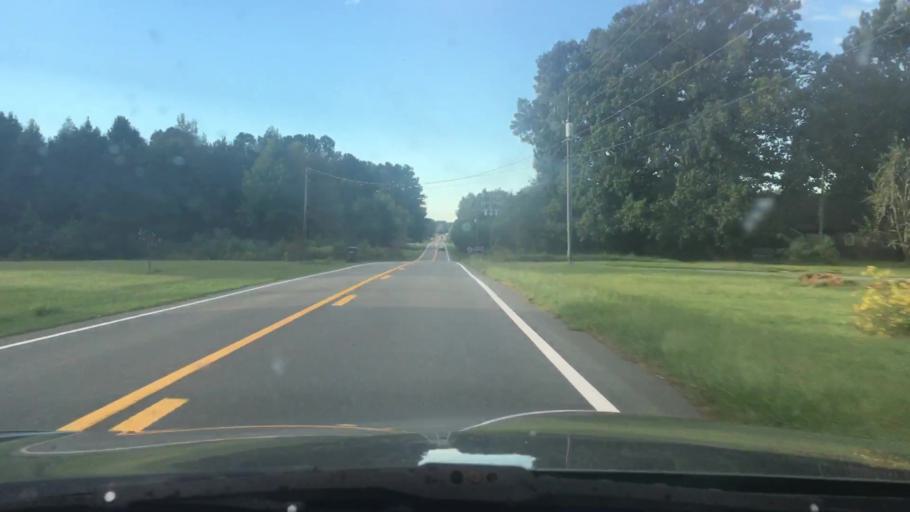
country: US
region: North Carolina
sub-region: Alamance County
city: Green Level
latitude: 36.2106
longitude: -79.3218
